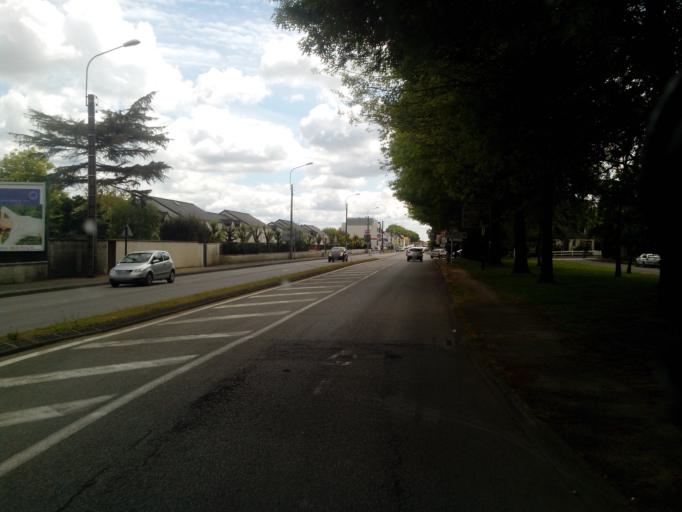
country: FR
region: Pays de la Loire
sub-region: Departement de la Loire-Atlantique
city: Orvault
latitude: 47.2600
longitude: -1.5817
